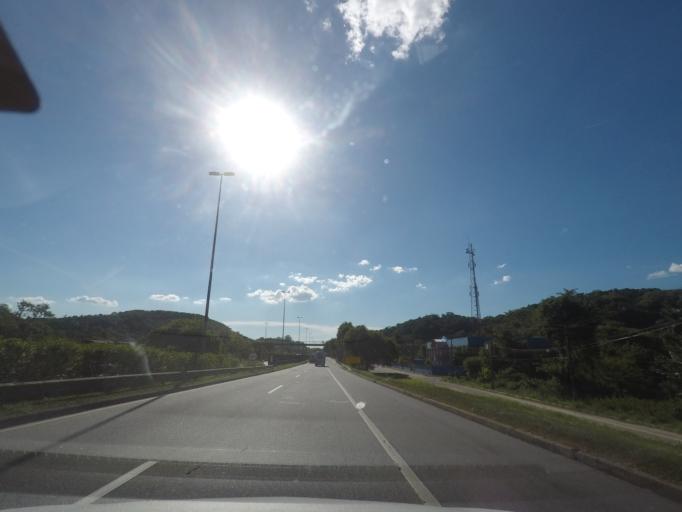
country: BR
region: Rio de Janeiro
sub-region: Petropolis
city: Petropolis
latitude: -22.6536
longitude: -43.1501
